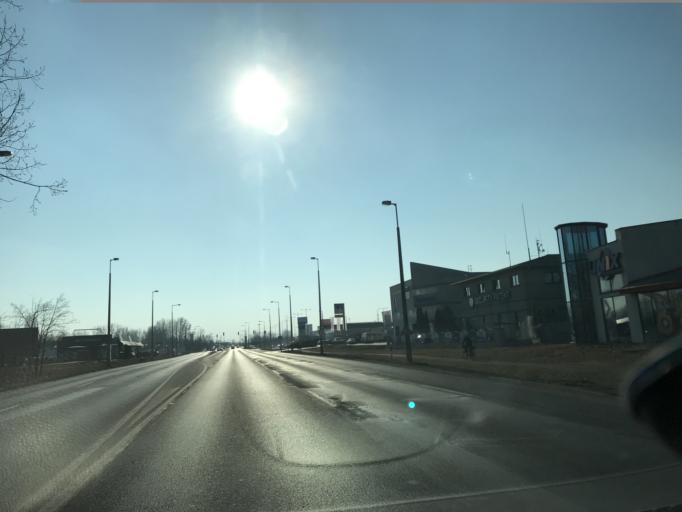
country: HU
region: Gyor-Moson-Sopron
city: Gyor
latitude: 47.6583
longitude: 17.6358
